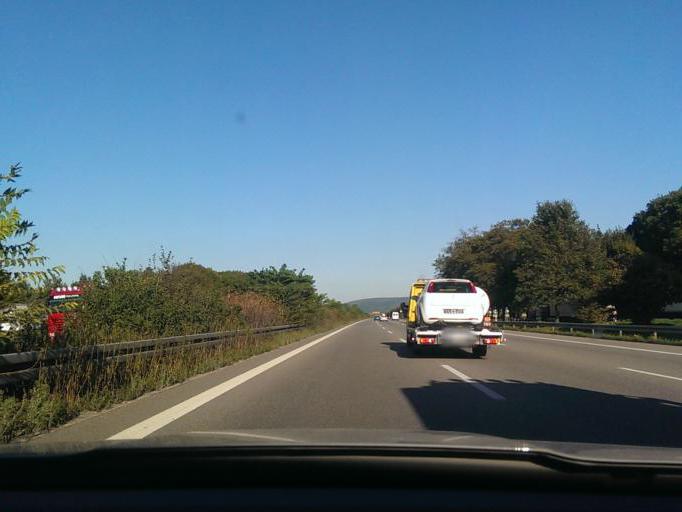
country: DE
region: Baden-Wuerttemberg
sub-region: Karlsruhe Region
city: Muggensturm
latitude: 48.8884
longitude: 8.2882
